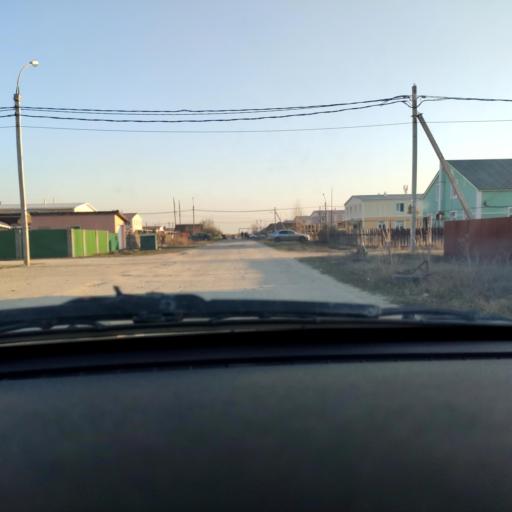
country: RU
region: Samara
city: Podstepki
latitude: 53.5716
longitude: 49.1192
